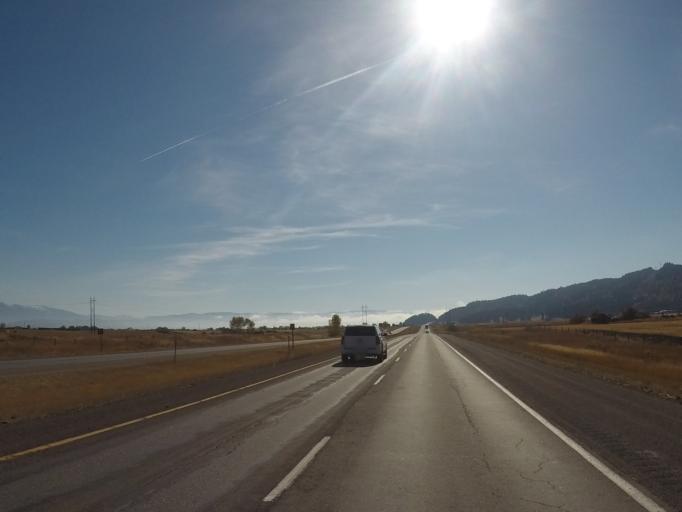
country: US
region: Montana
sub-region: Flathead County
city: Somers
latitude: 48.1165
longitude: -114.2549
